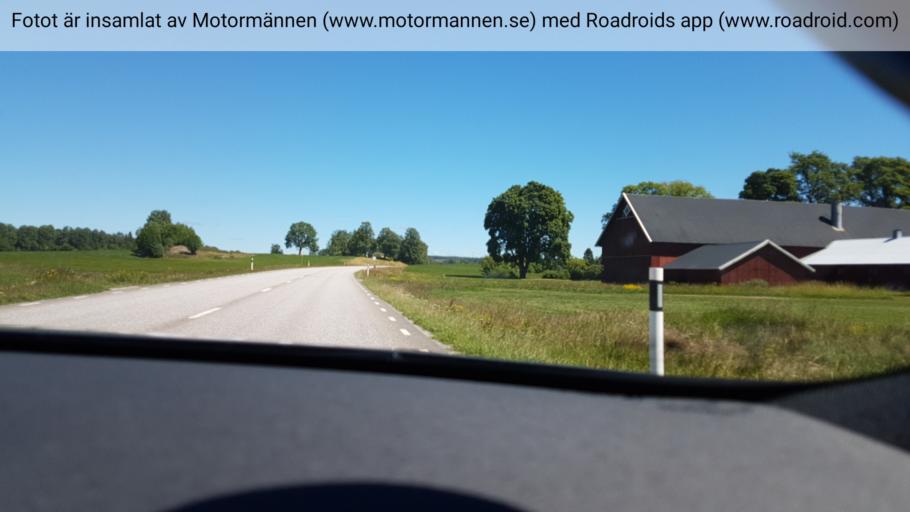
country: SE
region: Vaestra Goetaland
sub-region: Ulricehamns Kommun
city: Ulricehamn
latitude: 57.8916
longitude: 13.4415
